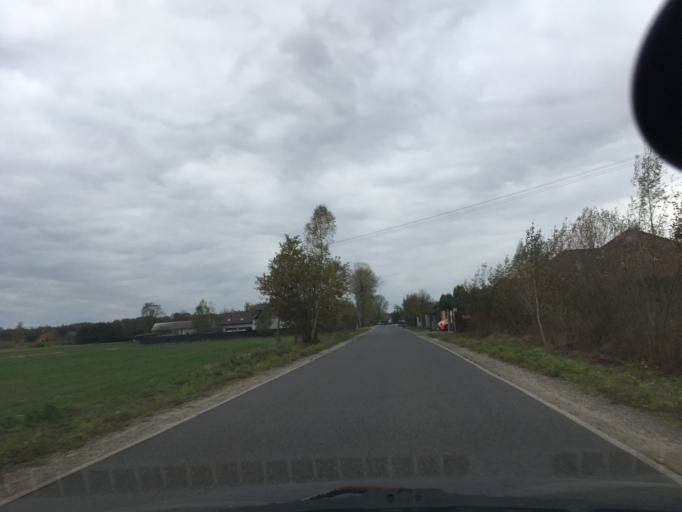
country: PL
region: Lodz Voivodeship
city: Zabia Wola
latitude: 52.0281
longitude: 20.6987
